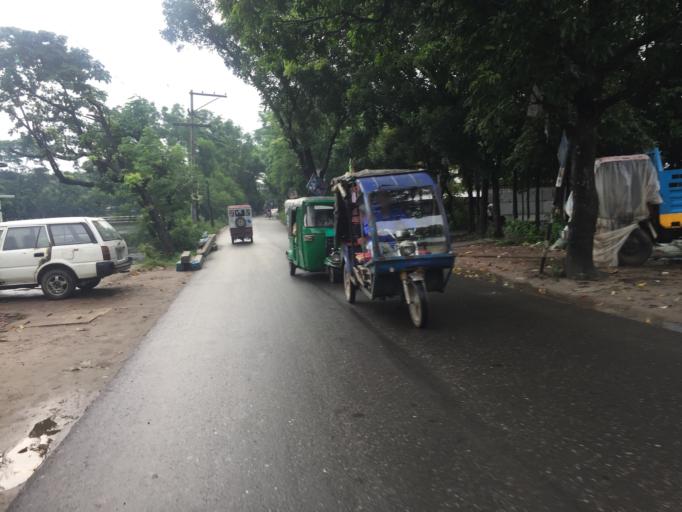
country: BD
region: Dhaka
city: Narayanganj
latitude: 23.5511
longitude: 90.4989
